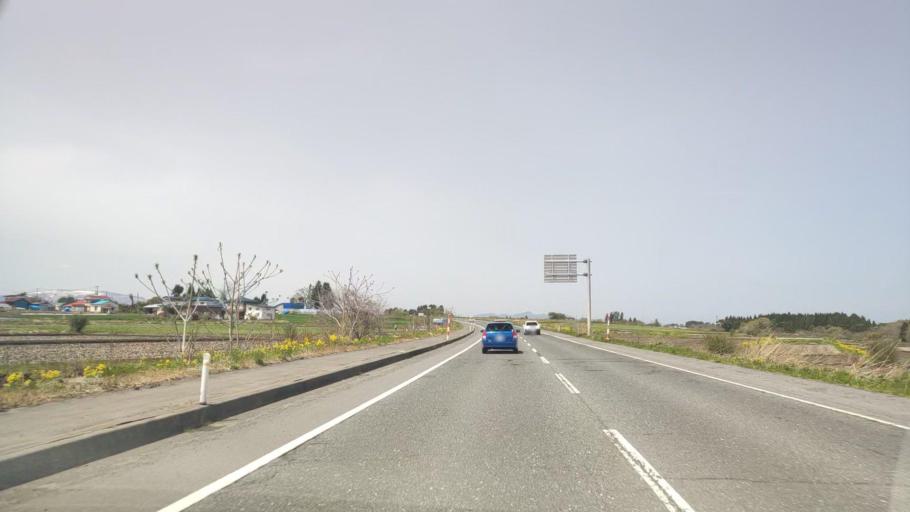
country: JP
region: Aomori
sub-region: Misawa Shi
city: Inuotose
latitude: 40.6350
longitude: 141.2441
